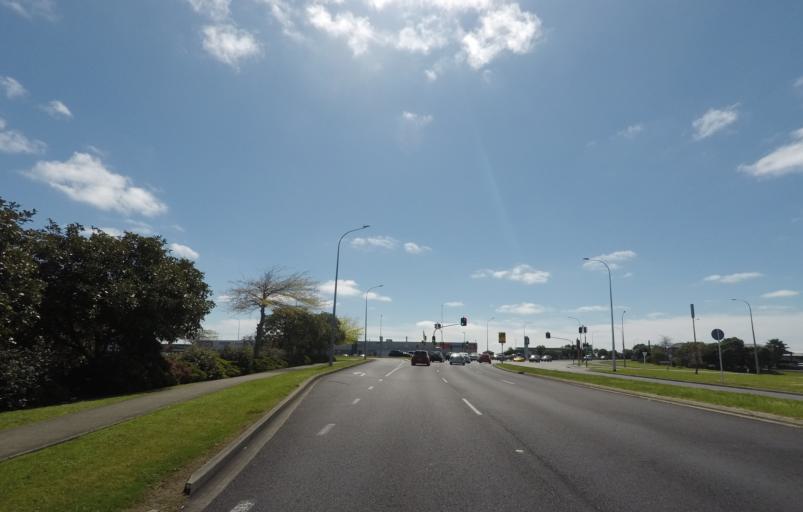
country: NZ
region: Auckland
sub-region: Auckland
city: Pakuranga
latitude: -36.9303
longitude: 174.9156
